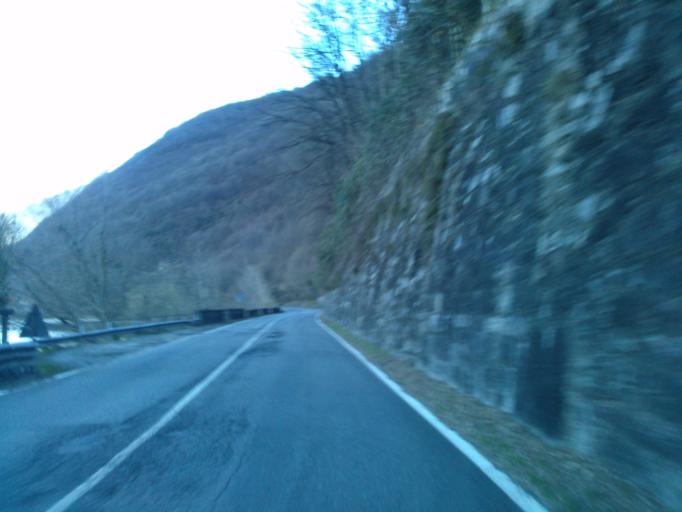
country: IT
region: Lombardy
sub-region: Provincia di Lecco
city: Dorio
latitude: 46.1167
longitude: 9.3410
